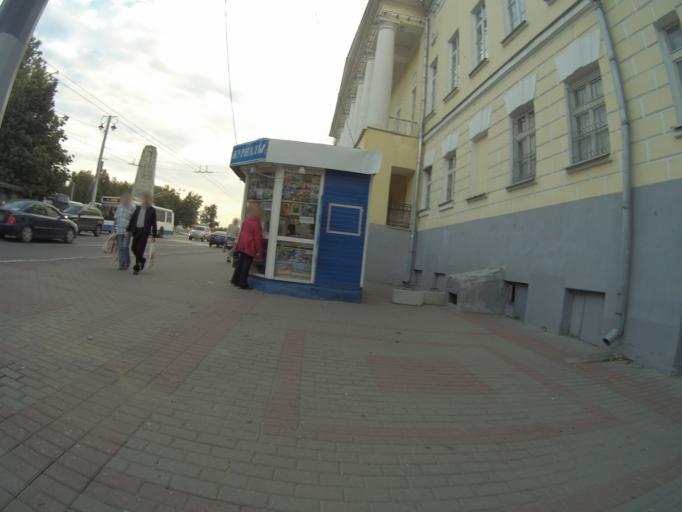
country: RU
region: Vladimir
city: Vladimir
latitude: 56.1297
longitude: 40.4084
